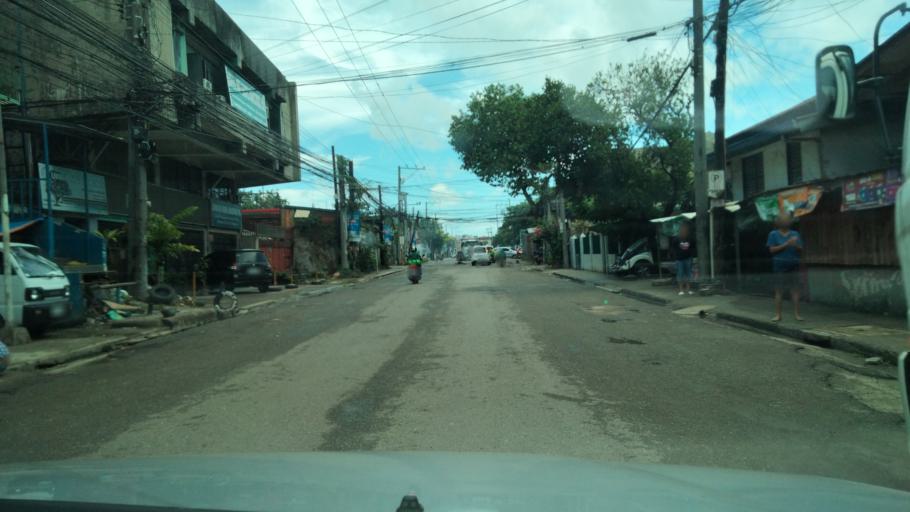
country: PH
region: Central Visayas
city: Mandaue City
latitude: 10.3291
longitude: 123.9319
